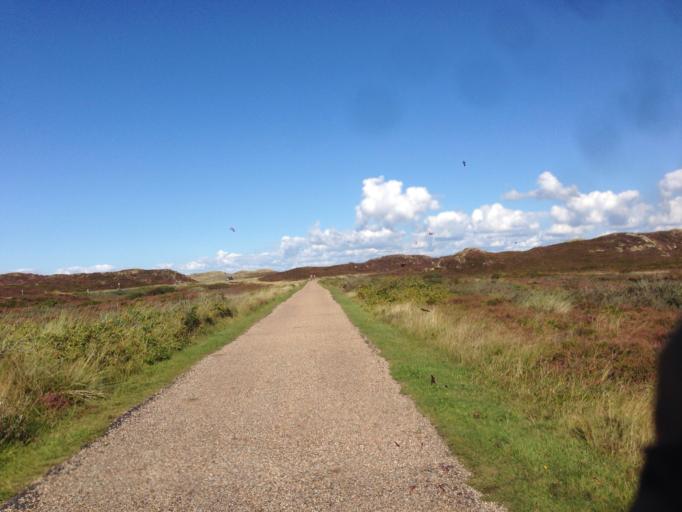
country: DE
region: Schleswig-Holstein
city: List
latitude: 55.0028
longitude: 8.3807
